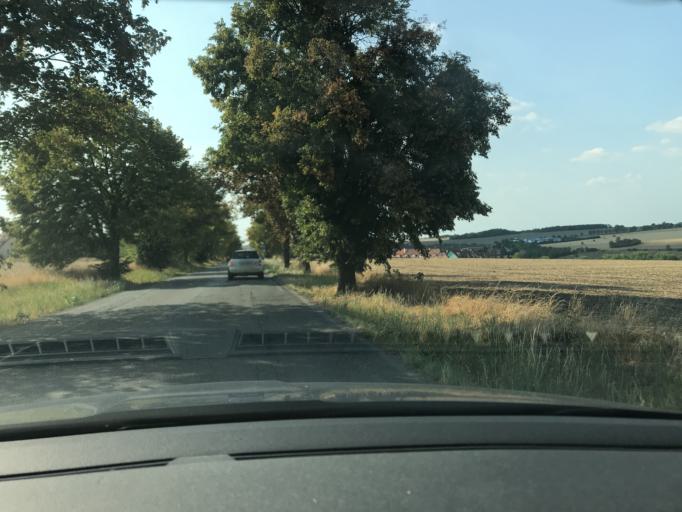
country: CZ
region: Central Bohemia
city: Velke Prilepy
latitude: 50.1562
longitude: 14.3246
